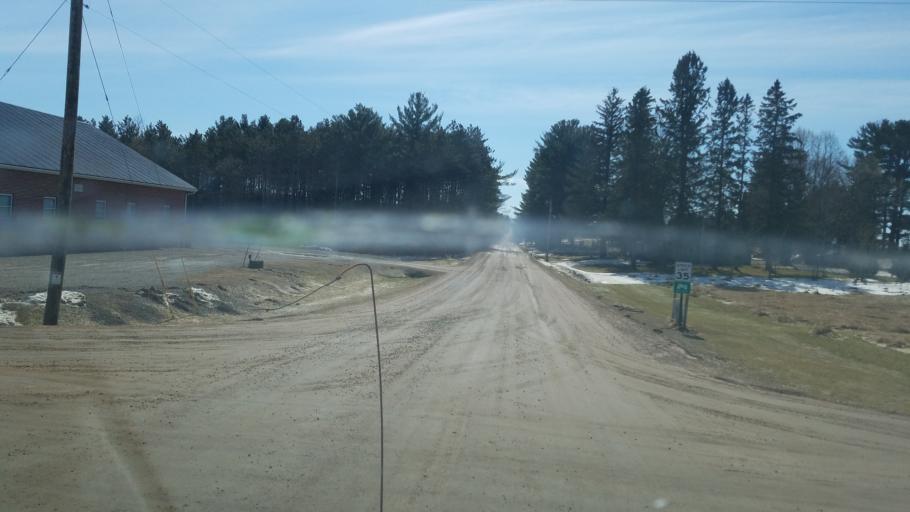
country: US
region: Wisconsin
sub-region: Clark County
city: Neillsville
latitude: 44.5965
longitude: -90.4565
